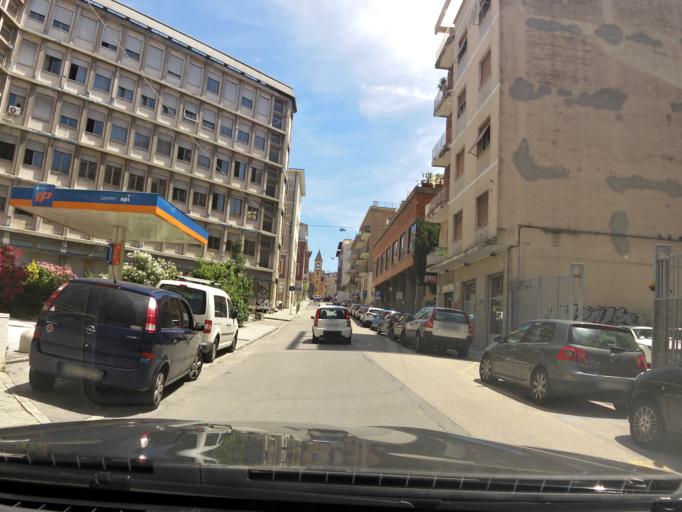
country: IT
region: The Marches
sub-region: Provincia di Ancona
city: Le Grazie di Ancona
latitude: 43.6156
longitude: 13.5164
